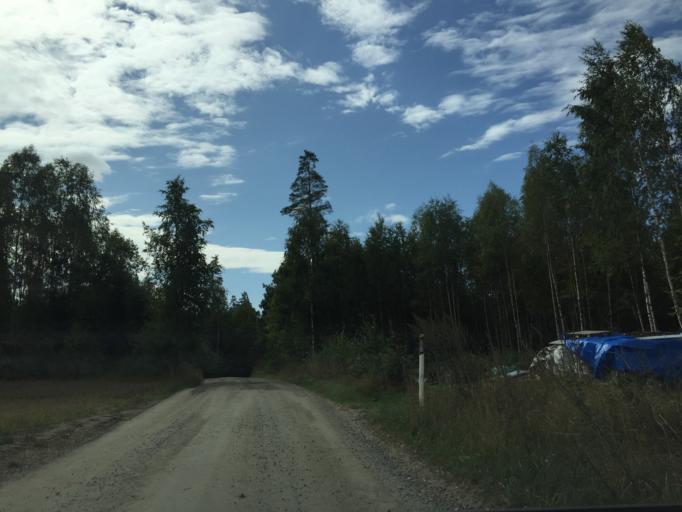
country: NO
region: Ostfold
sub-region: Hobol
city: Elvestad
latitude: 59.6440
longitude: 10.8904
